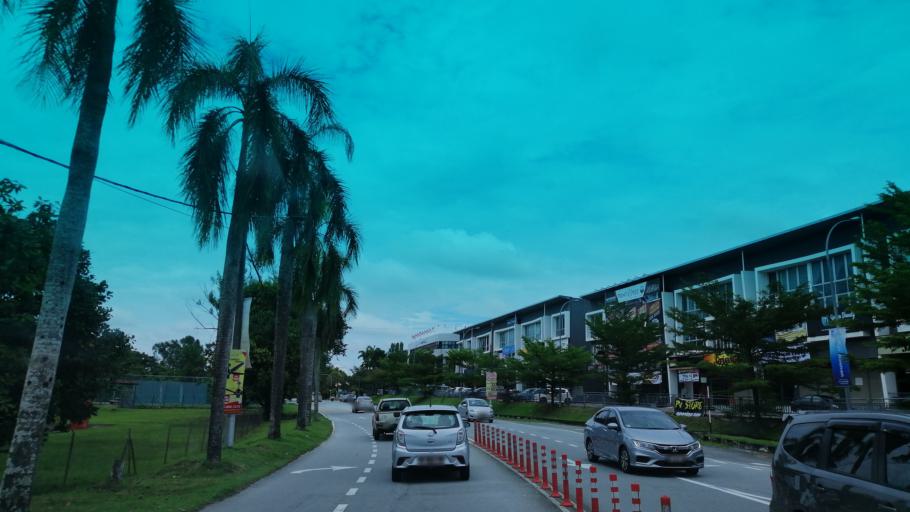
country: MY
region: Perak
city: Taiping
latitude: 4.8603
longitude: 100.7372
